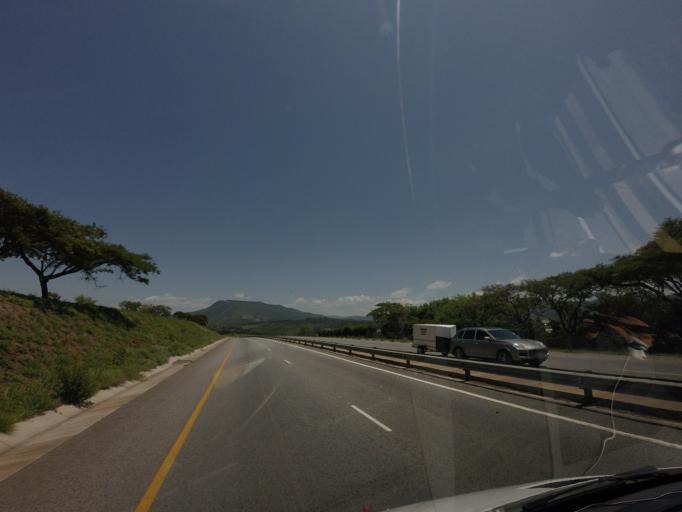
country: ZA
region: Mpumalanga
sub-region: Ehlanzeni District
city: Nelspruit
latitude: -25.4364
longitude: 30.8042
